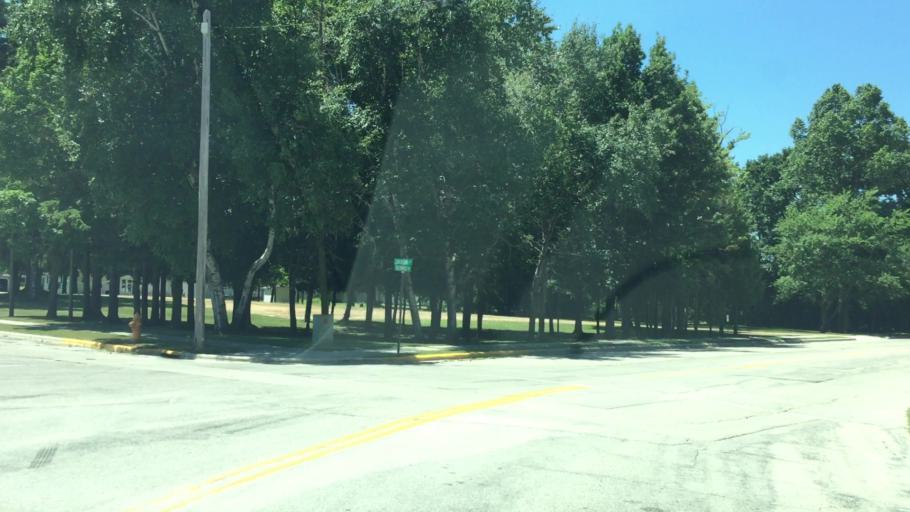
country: US
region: Wisconsin
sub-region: Calumet County
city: New Holstein
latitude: 43.9488
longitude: -88.0839
